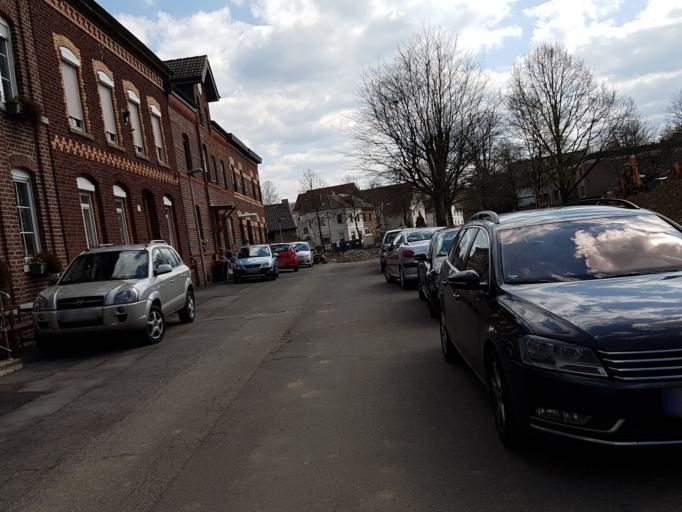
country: DE
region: North Rhine-Westphalia
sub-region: Regierungsbezirk Koln
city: Wurselen
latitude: 50.7879
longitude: 6.1557
